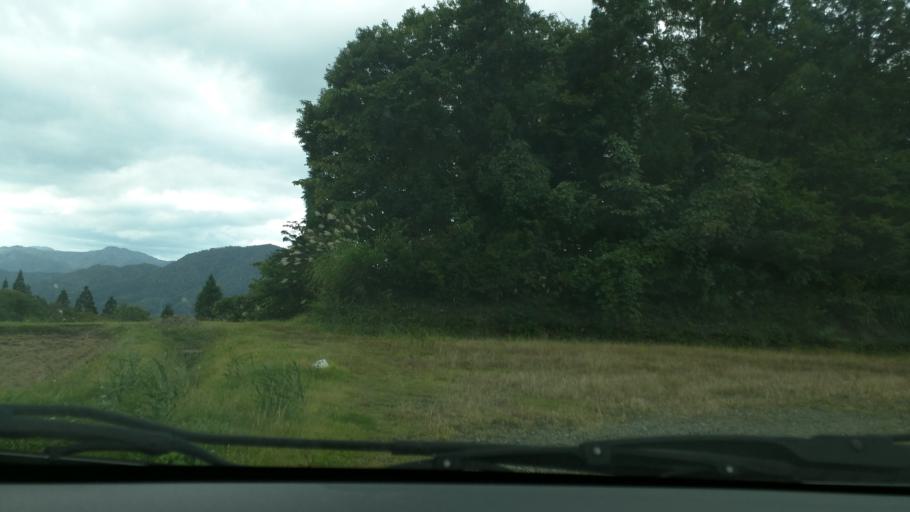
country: JP
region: Fukushima
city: Kitakata
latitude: 37.4594
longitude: 139.7265
